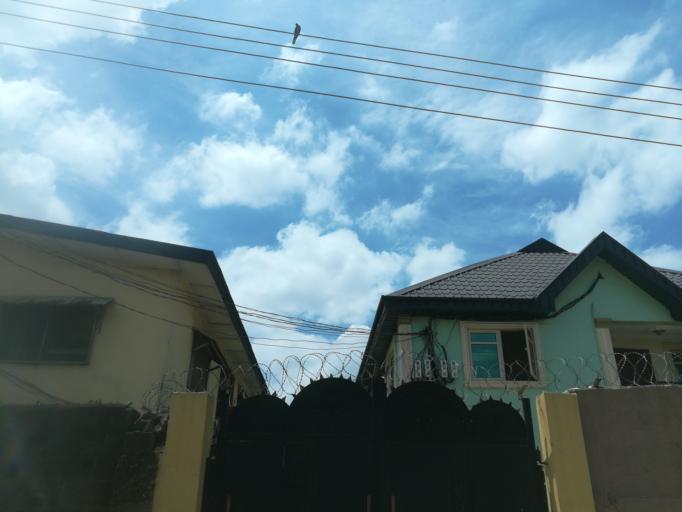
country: NG
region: Lagos
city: Oshodi
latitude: 6.5674
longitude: 3.3342
